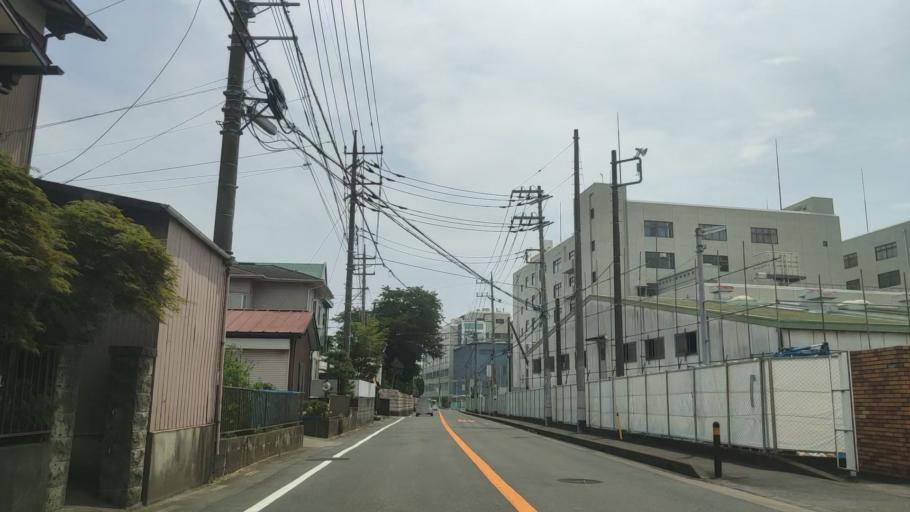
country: JP
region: Kanagawa
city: Atsugi
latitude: 35.4448
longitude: 139.3952
